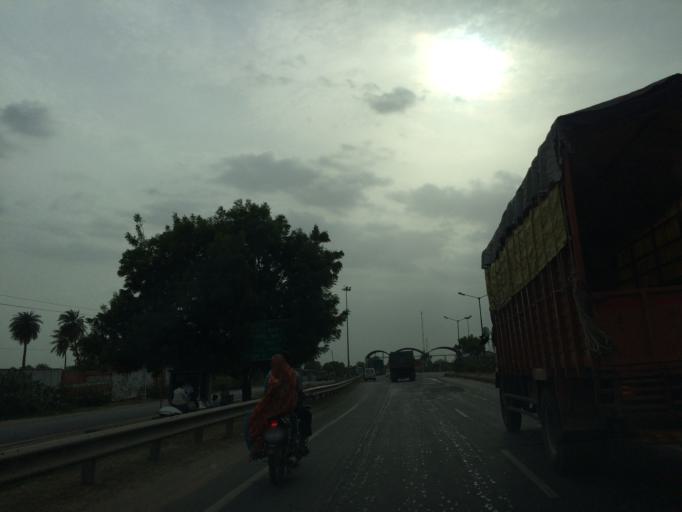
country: IN
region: Gujarat
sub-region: Ahmadabad
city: Sarkhej
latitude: 22.9345
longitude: 72.5221
